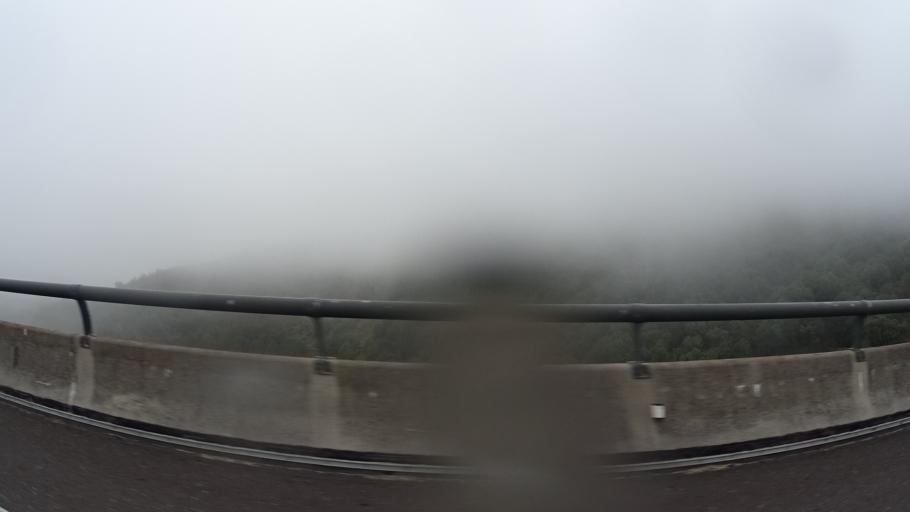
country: ES
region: Galicia
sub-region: Provincia de Lugo
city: Becerrea
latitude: 42.8469
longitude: -7.1210
